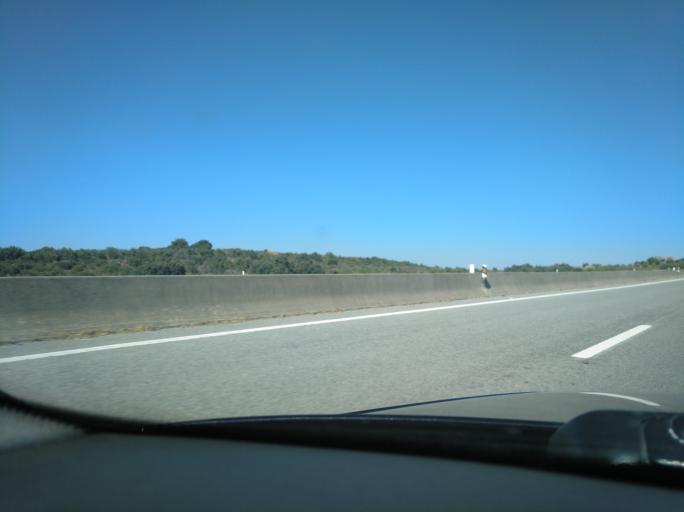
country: PT
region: Faro
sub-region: Tavira
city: Luz
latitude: 37.1354
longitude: -7.7434
